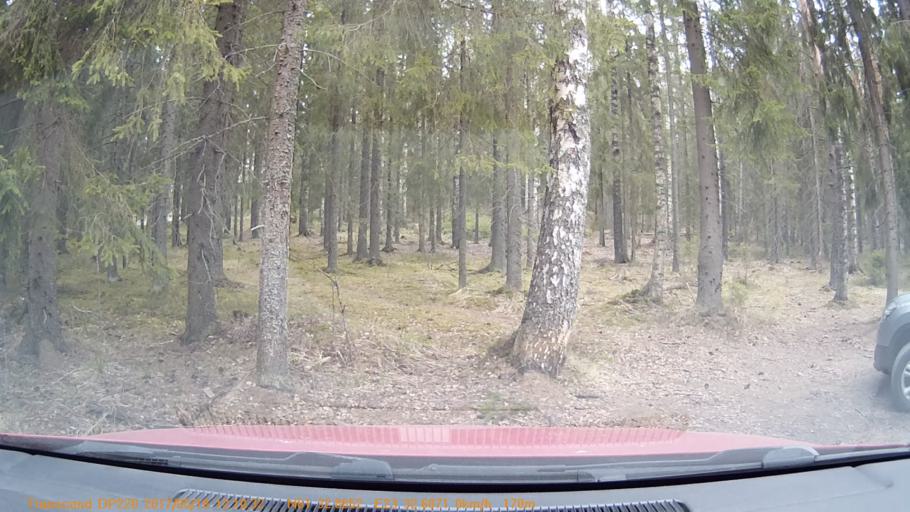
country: FI
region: Pirkanmaa
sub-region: Tampere
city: Yloejaervi
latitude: 61.5478
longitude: 23.5448
